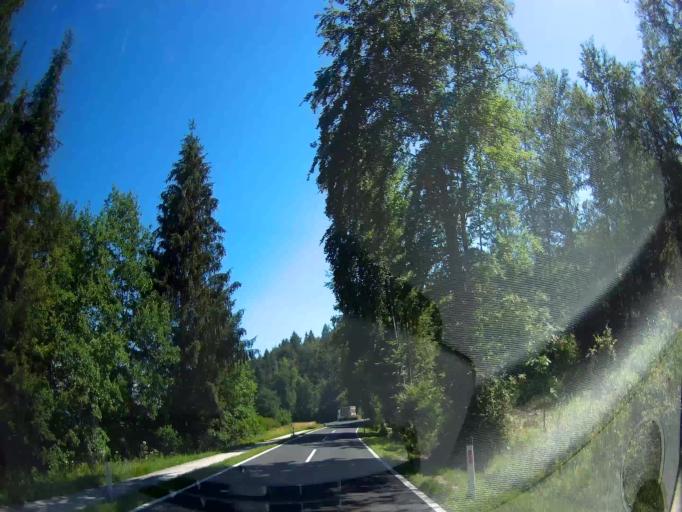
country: AT
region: Carinthia
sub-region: Politischer Bezirk Volkermarkt
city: Sittersdorf
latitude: 46.5580
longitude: 14.6215
